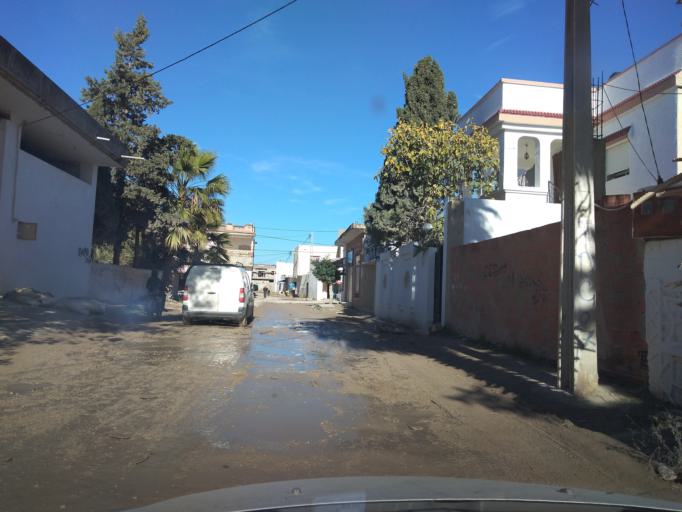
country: TN
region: Ariana
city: Qal'at al Andalus
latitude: 37.0613
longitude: 10.1226
